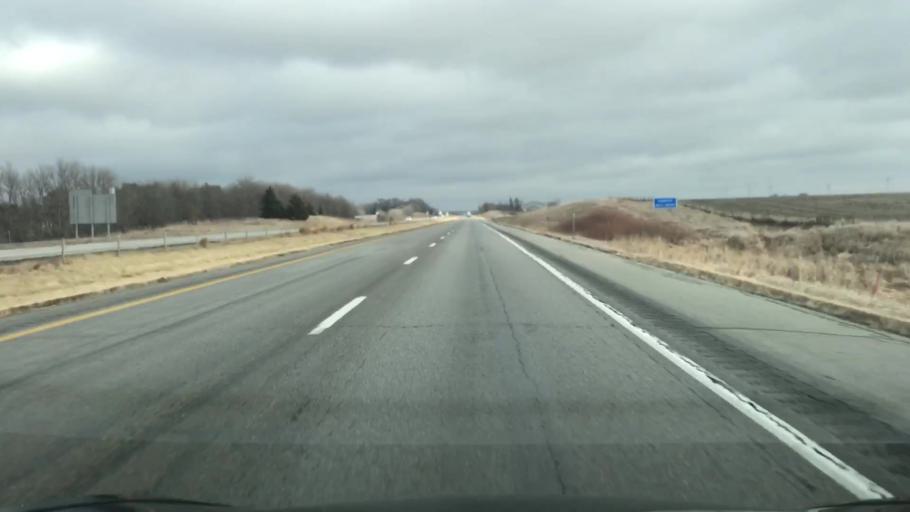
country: US
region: Iowa
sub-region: Guthrie County
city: Stuart
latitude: 41.4957
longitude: -94.4284
